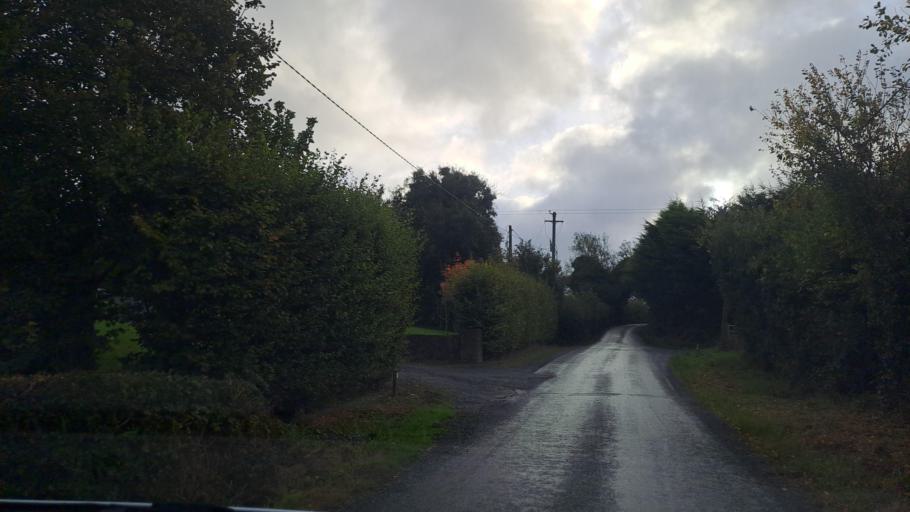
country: IE
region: Ulster
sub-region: An Cabhan
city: Kingscourt
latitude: 53.9577
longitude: -6.8045
